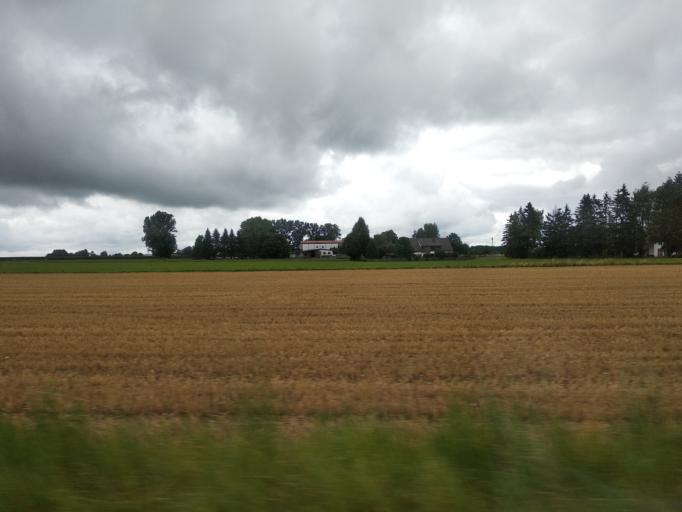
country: DE
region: Bavaria
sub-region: Swabia
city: Benningen
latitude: 47.9702
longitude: 10.2336
